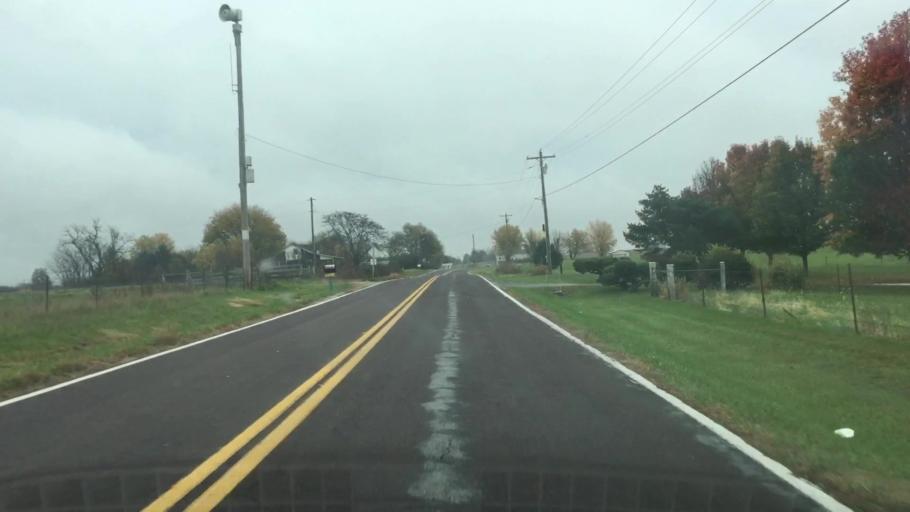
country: US
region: Missouri
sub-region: Callaway County
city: Fulton
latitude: 38.8257
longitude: -91.9111
